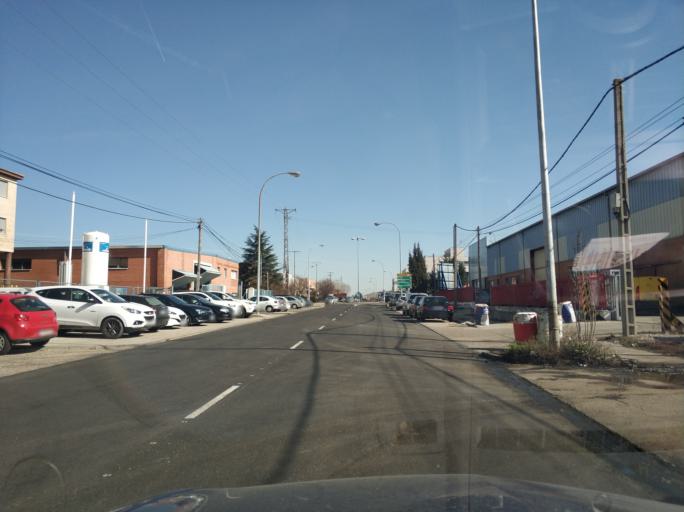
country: ES
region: Castille and Leon
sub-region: Provincia de Valladolid
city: Cisterniga
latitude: 41.6169
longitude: -4.7074
